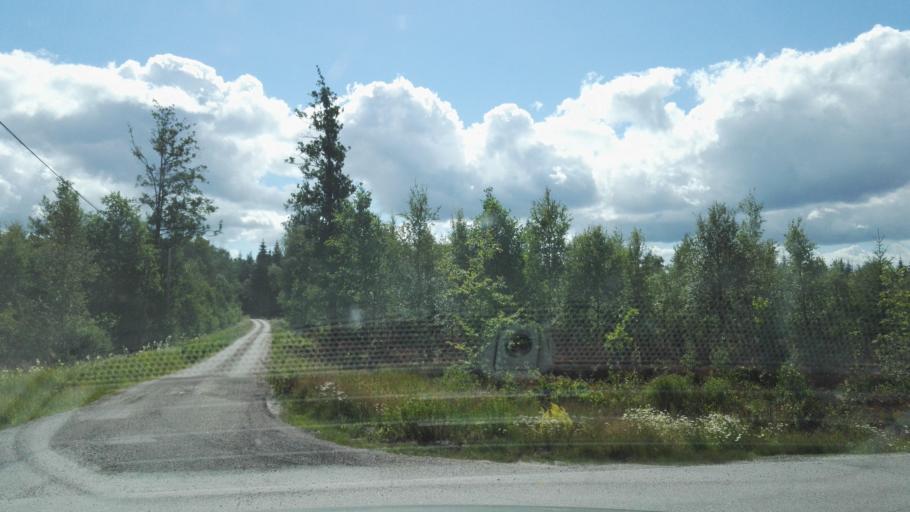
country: SE
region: Kronoberg
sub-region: Vaxjo Kommun
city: Gemla
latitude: 56.8914
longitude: 14.6939
